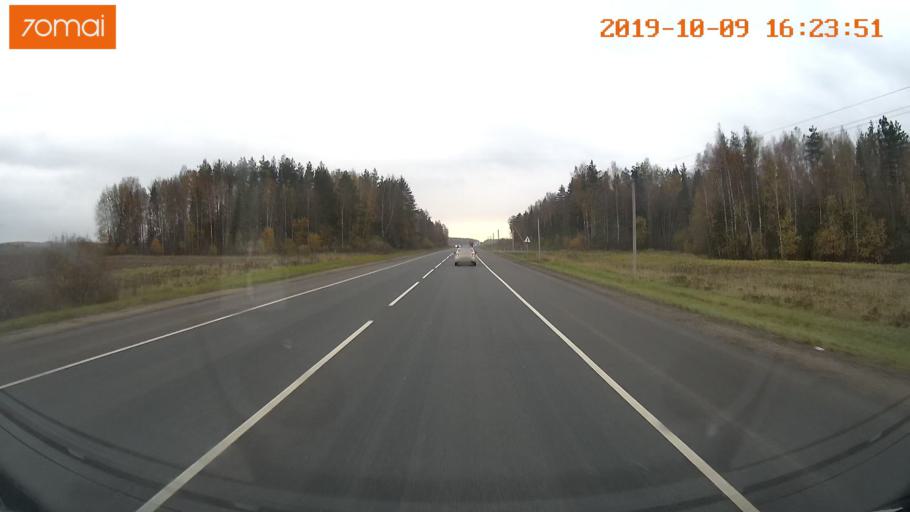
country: RU
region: Kostroma
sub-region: Kostromskoy Rayon
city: Kostroma
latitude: 57.6588
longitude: 40.9044
